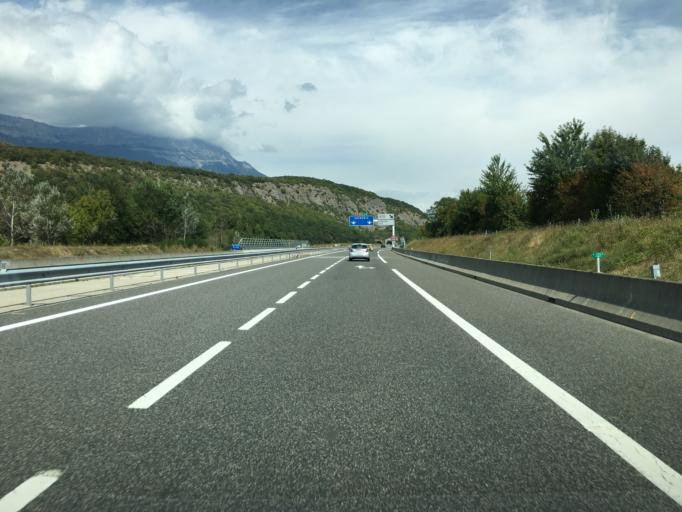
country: FR
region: Rhone-Alpes
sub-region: Departement de l'Isere
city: Vif
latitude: 45.0717
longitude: 5.6799
